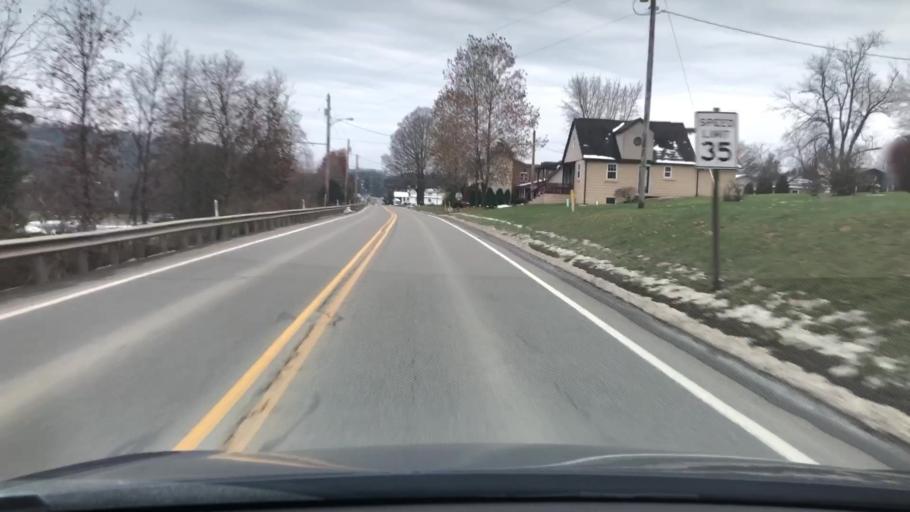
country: US
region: Pennsylvania
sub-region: Clarion County
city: Clarion
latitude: 41.0220
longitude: -79.2695
